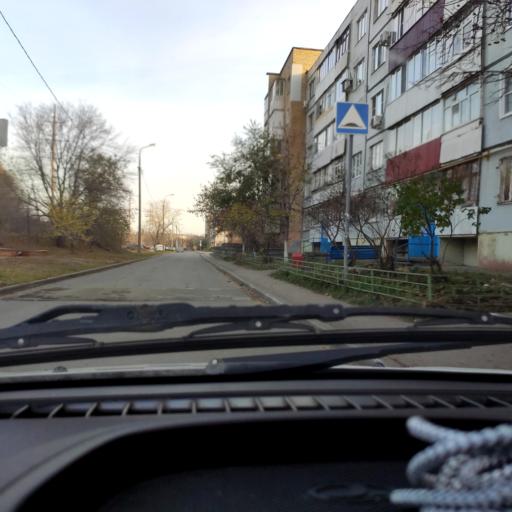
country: RU
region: Samara
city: Zhigulevsk
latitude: 53.4736
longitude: 49.5341
